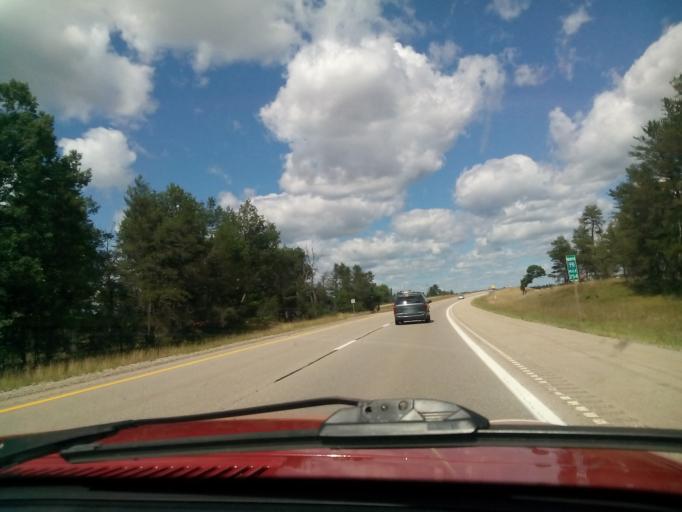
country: US
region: Michigan
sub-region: Crawford County
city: Grayling
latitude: 44.6477
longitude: -84.7055
